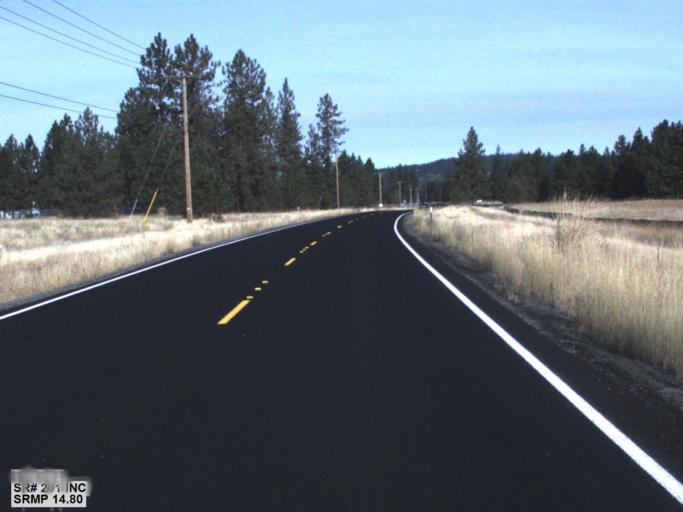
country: US
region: Washington
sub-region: Spokane County
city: Deer Park
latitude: 47.8251
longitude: -117.5930
